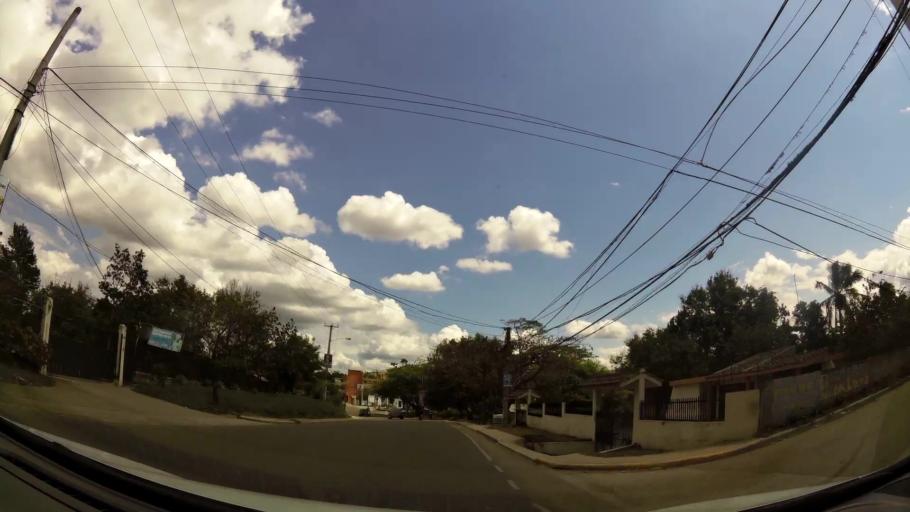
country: DO
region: Santiago
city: Santiago de los Caballeros
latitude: 19.4142
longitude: -70.6768
